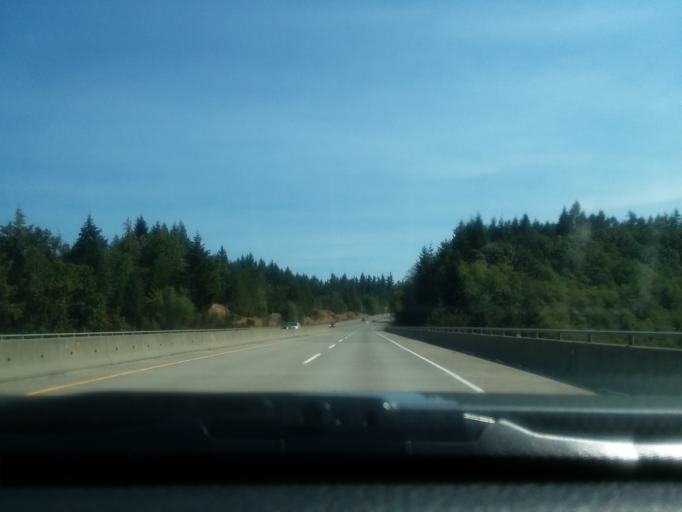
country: CA
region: British Columbia
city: Port Alberni
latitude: 49.3862
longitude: -124.6333
